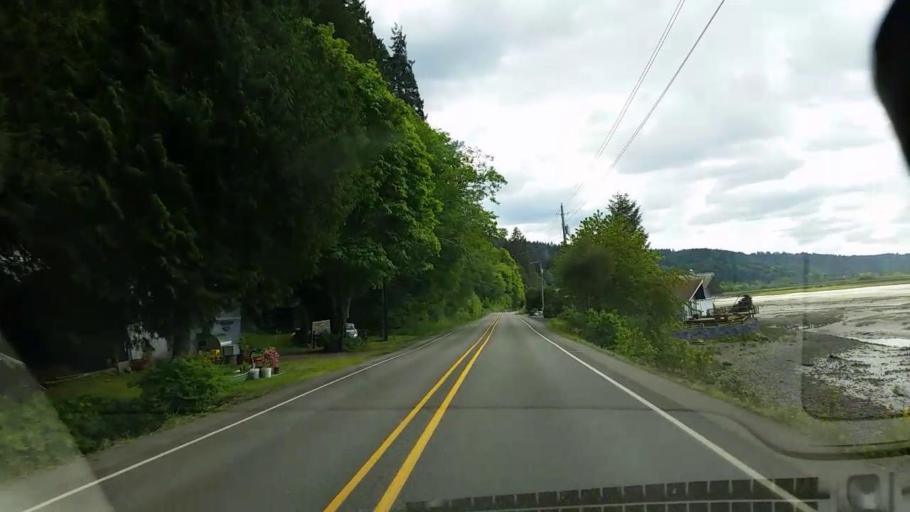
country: US
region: Washington
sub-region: Mason County
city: Shelton
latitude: 47.3461
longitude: -123.1086
